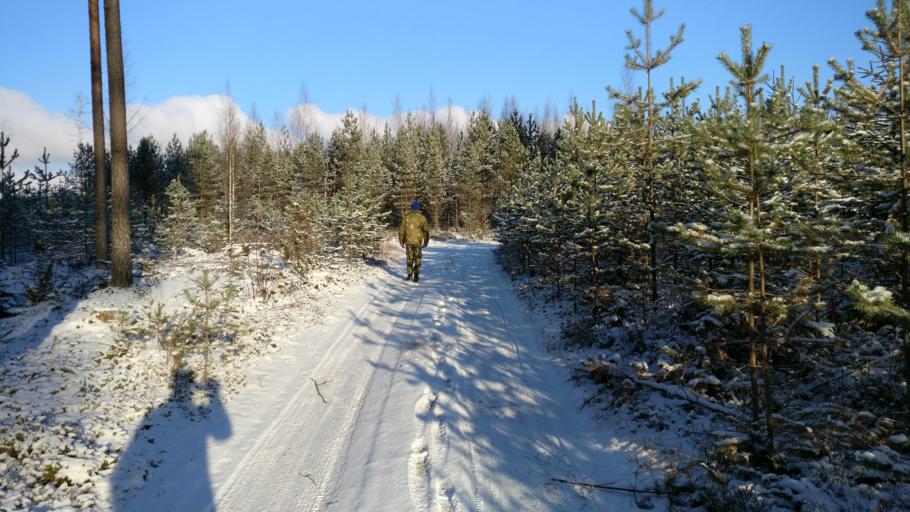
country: FI
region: Central Finland
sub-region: Jyvaeskylae
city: Hankasalmi
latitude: 62.4236
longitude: 26.6747
